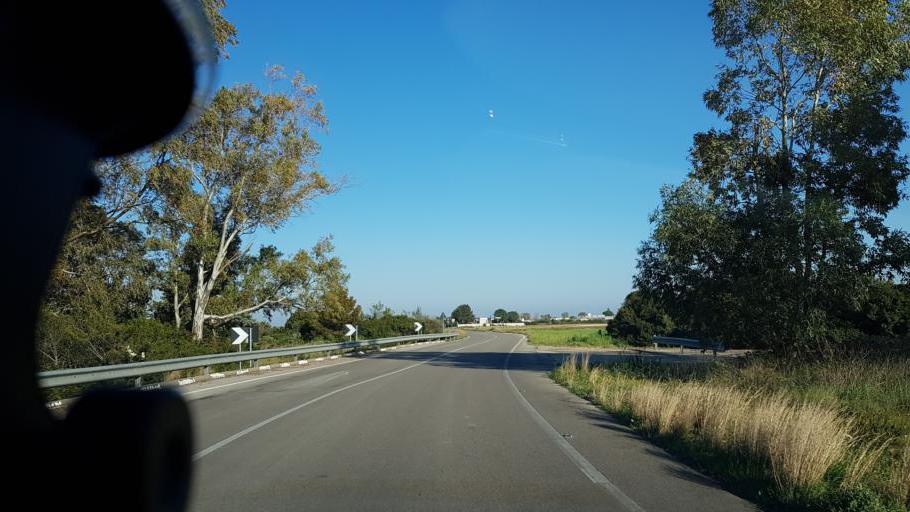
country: IT
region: Apulia
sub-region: Provincia di Lecce
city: Struda
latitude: 40.3946
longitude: 18.2699
